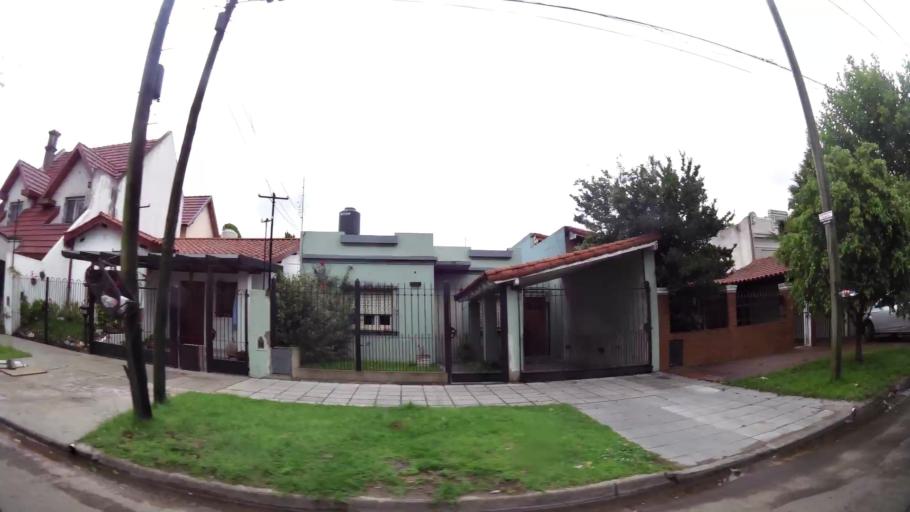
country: AR
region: Buenos Aires
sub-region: Partido de Lomas de Zamora
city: Lomas de Zamora
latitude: -34.7476
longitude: -58.3851
